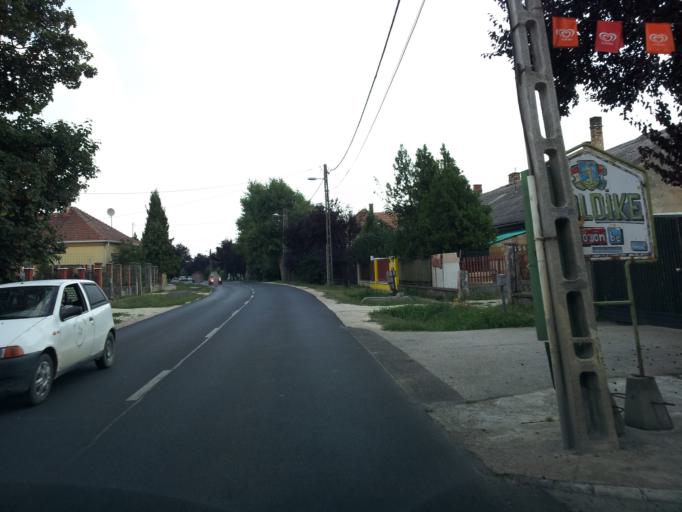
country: HU
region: Pest
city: Toekoel
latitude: 47.3300
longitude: 18.9648
